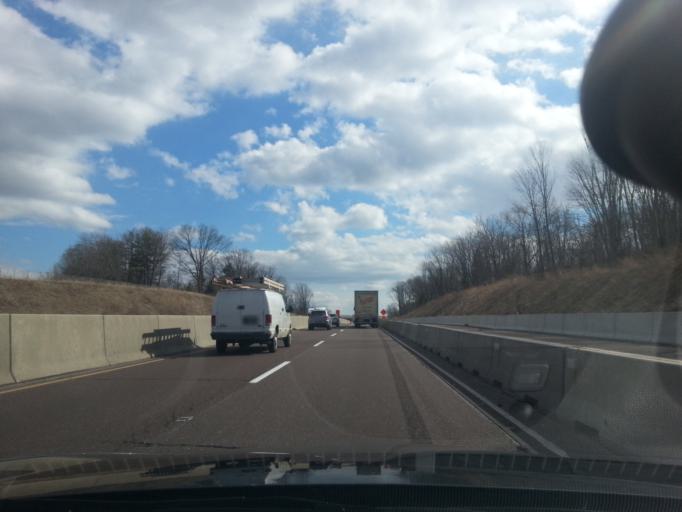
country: US
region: Pennsylvania
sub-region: Montgomery County
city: North Wales
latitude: 40.1929
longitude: -75.3154
